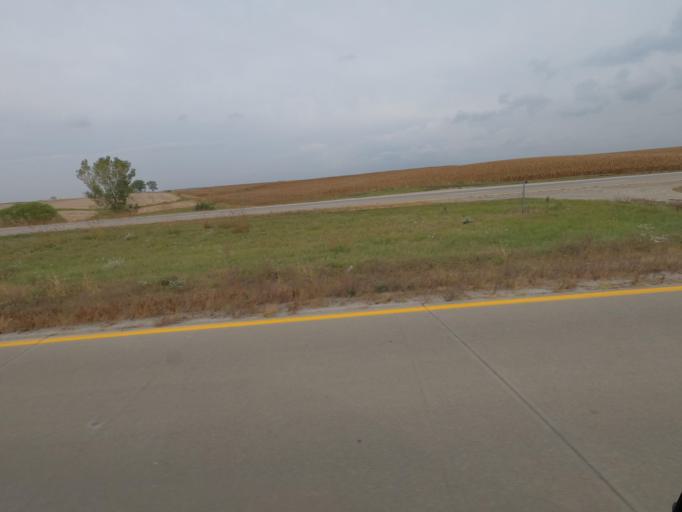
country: US
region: Iowa
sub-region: Mahaska County
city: Oskaloosa
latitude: 41.3306
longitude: -92.7181
